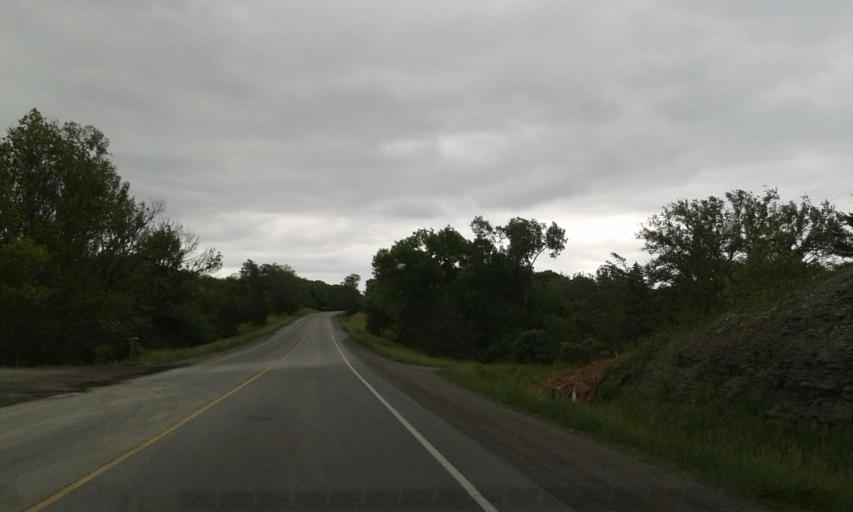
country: CA
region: Ontario
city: Quinte West
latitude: 43.9781
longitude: -77.5085
